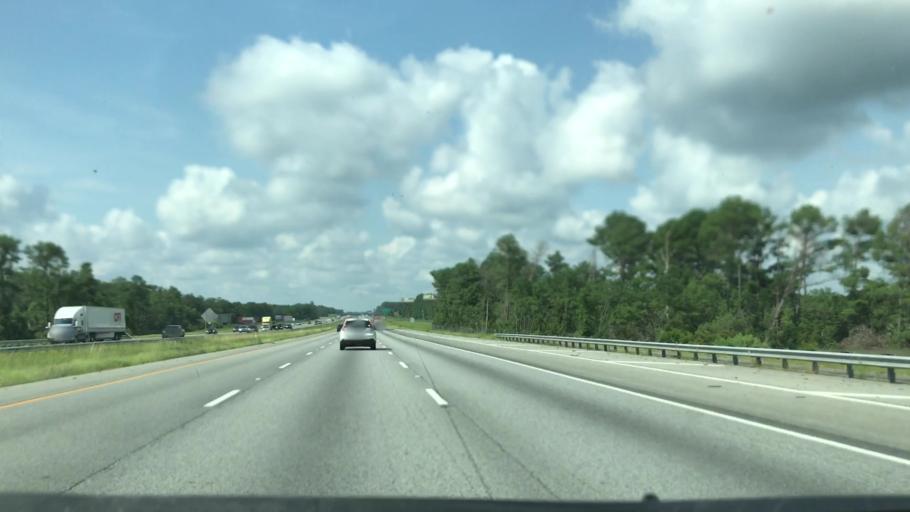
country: US
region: Georgia
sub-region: Glynn County
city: Brunswick
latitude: 31.1165
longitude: -81.5887
